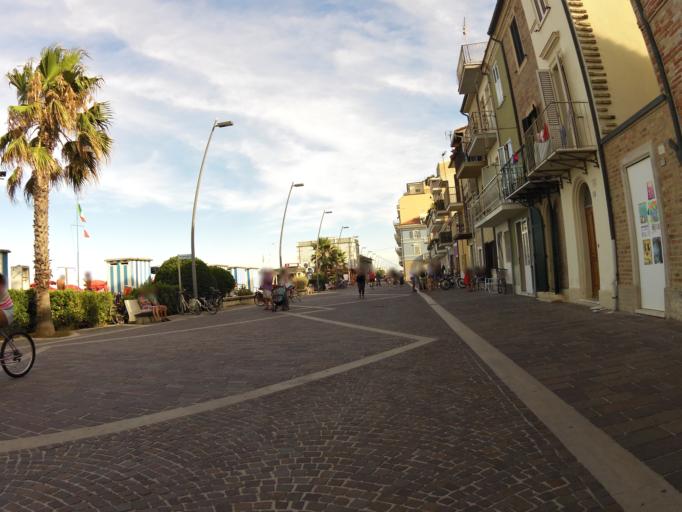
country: IT
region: The Marches
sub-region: Provincia di Macerata
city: Porto Recanati
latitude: 43.4314
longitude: 13.6663
